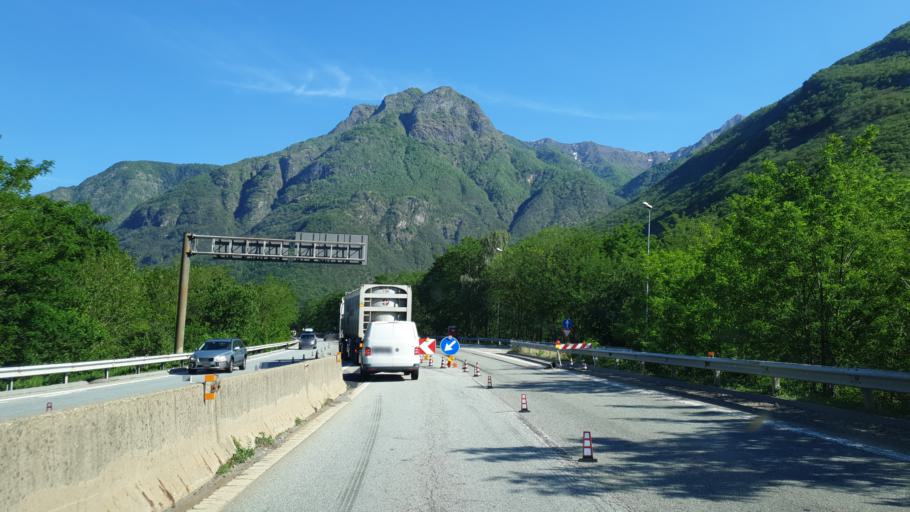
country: IT
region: Piedmont
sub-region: Provincia Verbano-Cusio-Ossola
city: Vogogna
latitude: 46.0017
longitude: 8.2809
